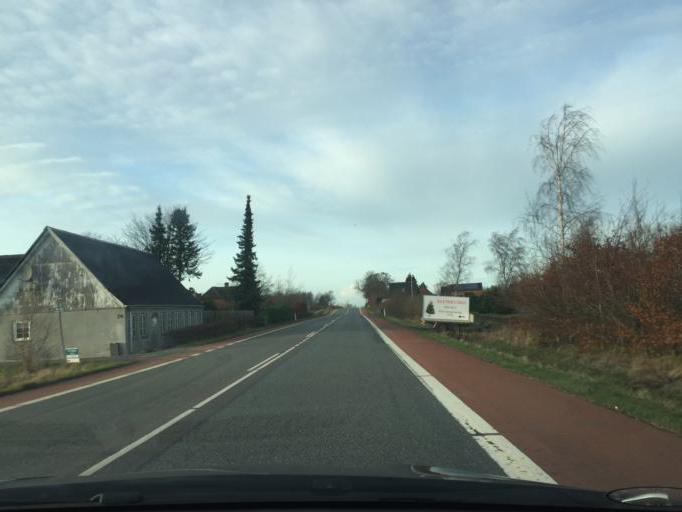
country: DK
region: South Denmark
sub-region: Faaborg-Midtfyn Kommune
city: Ringe
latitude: 55.2662
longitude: 10.4565
